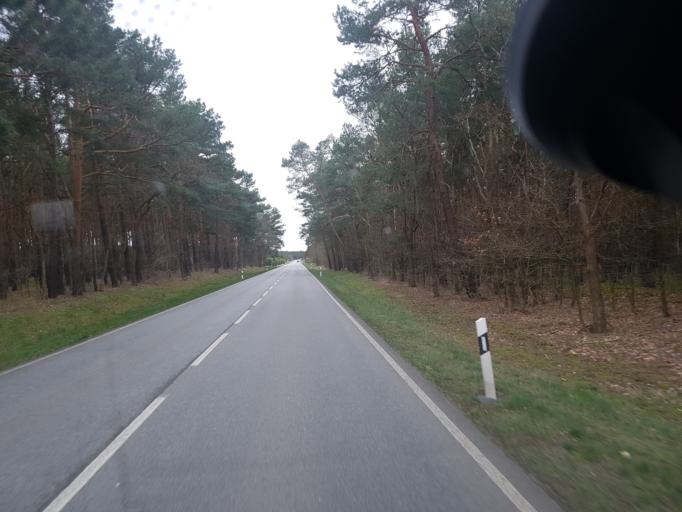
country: DE
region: Brandenburg
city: Luebben
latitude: 51.9165
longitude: 13.8688
